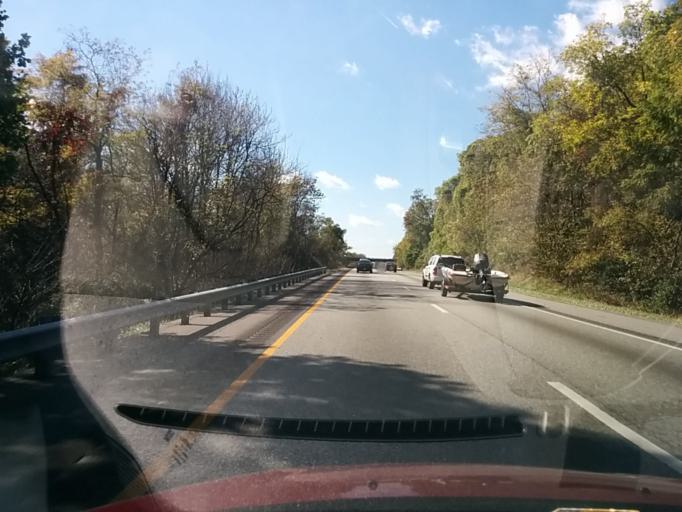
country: US
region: Virginia
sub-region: Botetourt County
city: Daleville
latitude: 37.4229
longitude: -79.8807
